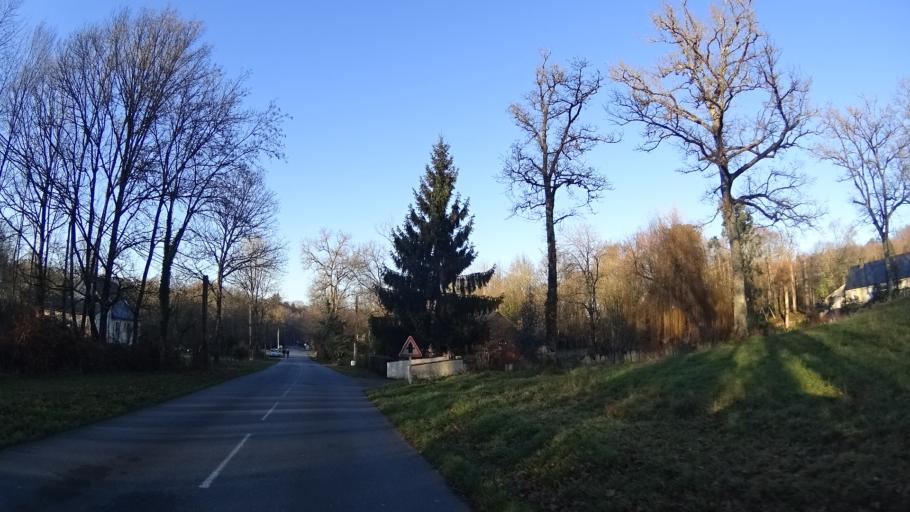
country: FR
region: Brittany
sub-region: Departement du Morbihan
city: Saint-Jean-la-Poterie
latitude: 47.6387
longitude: -2.1220
